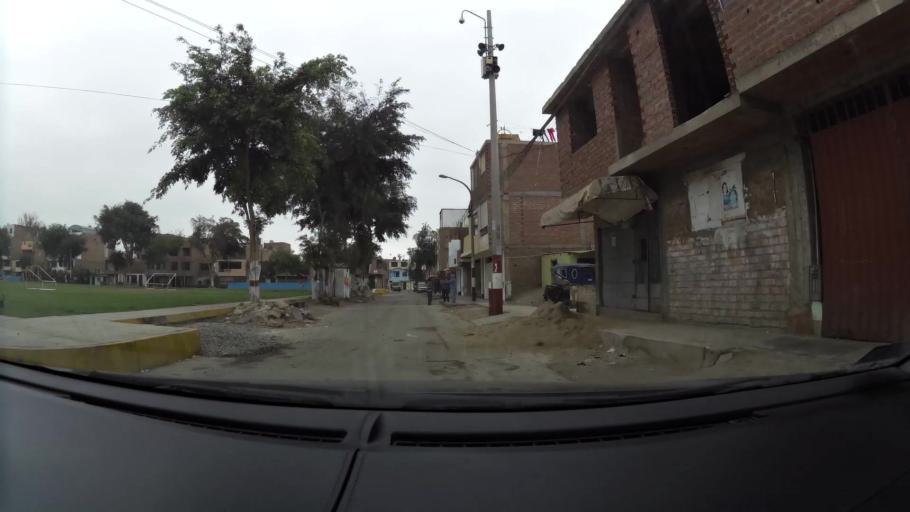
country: PE
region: Lima
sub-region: Lima
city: Independencia
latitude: -11.9656
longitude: -77.0771
